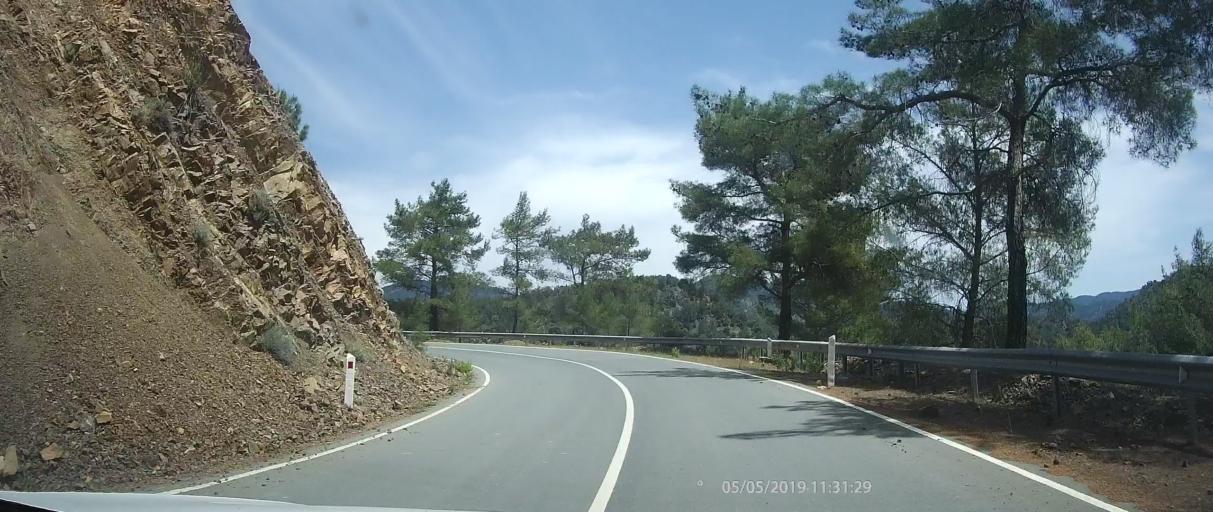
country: CY
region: Limassol
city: Pachna
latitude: 34.9495
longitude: 32.6469
